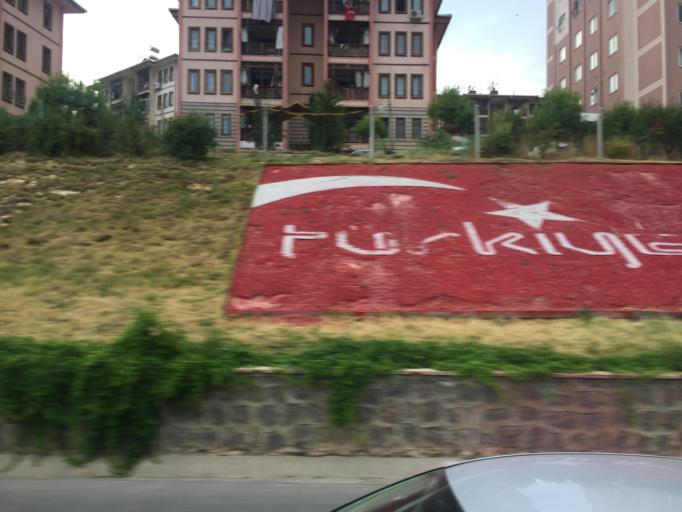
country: TR
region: Gaziantep
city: Gaziantep
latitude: 37.0431
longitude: 37.4246
